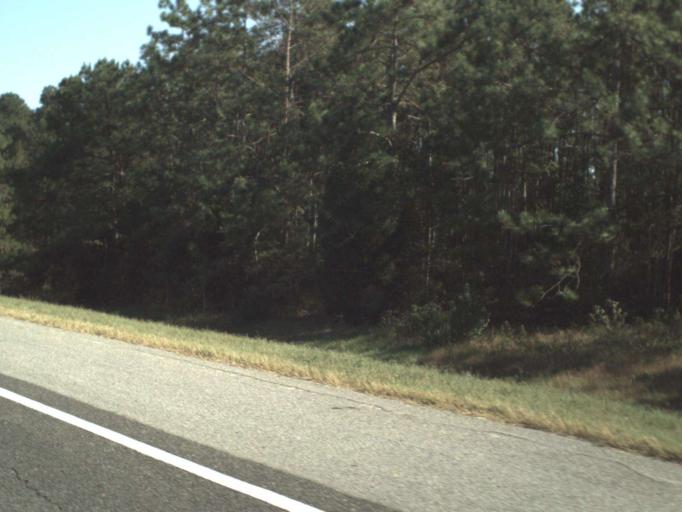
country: US
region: Florida
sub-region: Washington County
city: Chipley
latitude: 30.7465
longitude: -85.5438
